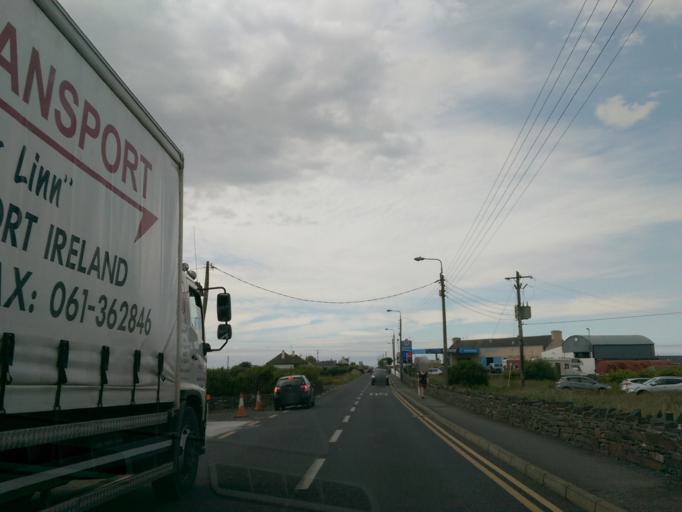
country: IE
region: Munster
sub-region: An Clar
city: Kilrush
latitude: 52.8576
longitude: -9.4026
